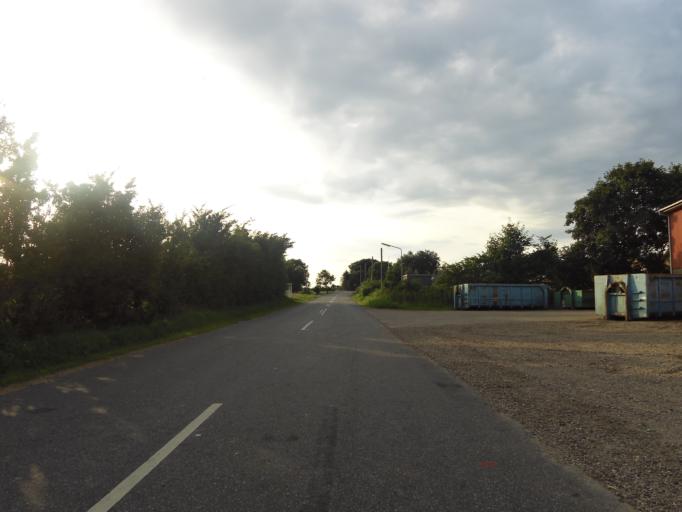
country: DK
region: South Denmark
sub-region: Tonder Kommune
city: Sherrebek
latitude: 55.2099
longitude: 8.8862
